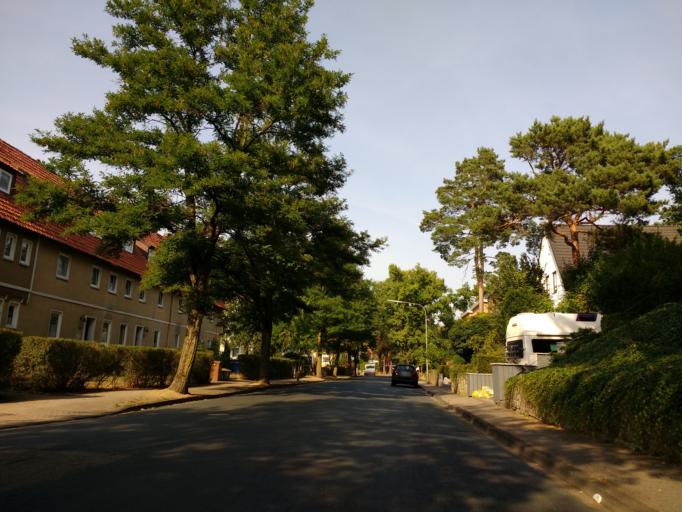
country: DE
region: Lower Saxony
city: Gifhorn
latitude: 52.4736
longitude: 10.5376
